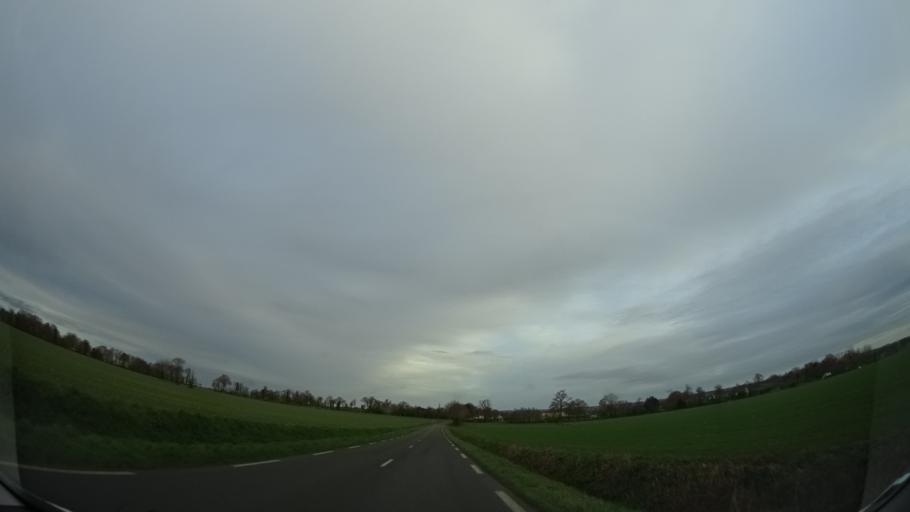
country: FR
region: Brittany
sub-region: Departement des Cotes-d'Armor
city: Evran
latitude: 48.3592
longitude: -1.9695
